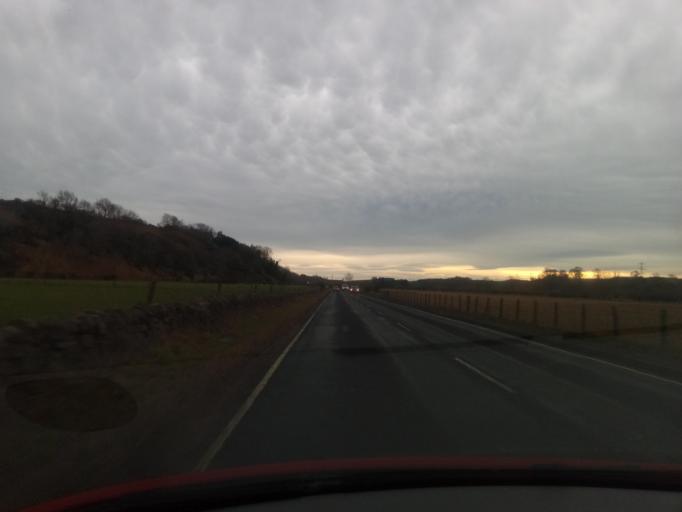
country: GB
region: England
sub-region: Northumberland
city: Wooler
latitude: 55.5366
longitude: -2.0030
